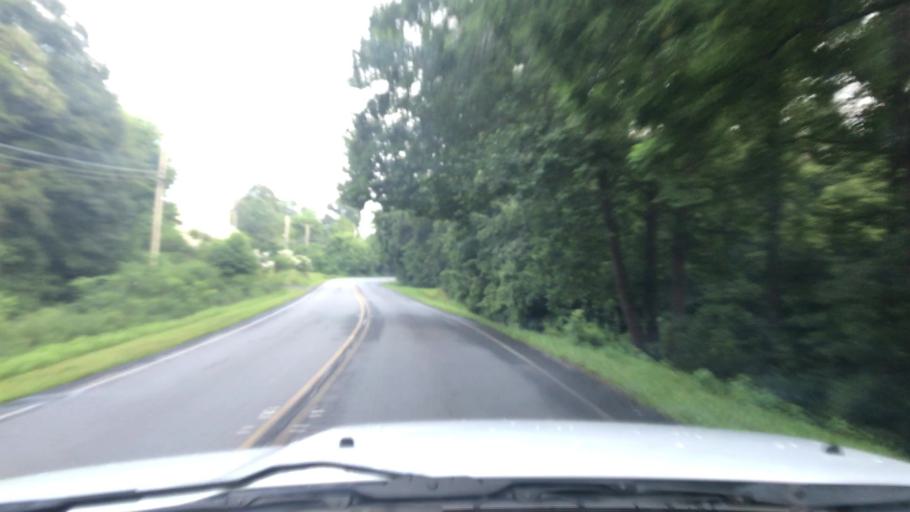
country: US
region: Georgia
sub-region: Fannin County
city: Blue Ridge
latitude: 34.9055
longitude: -84.2679
